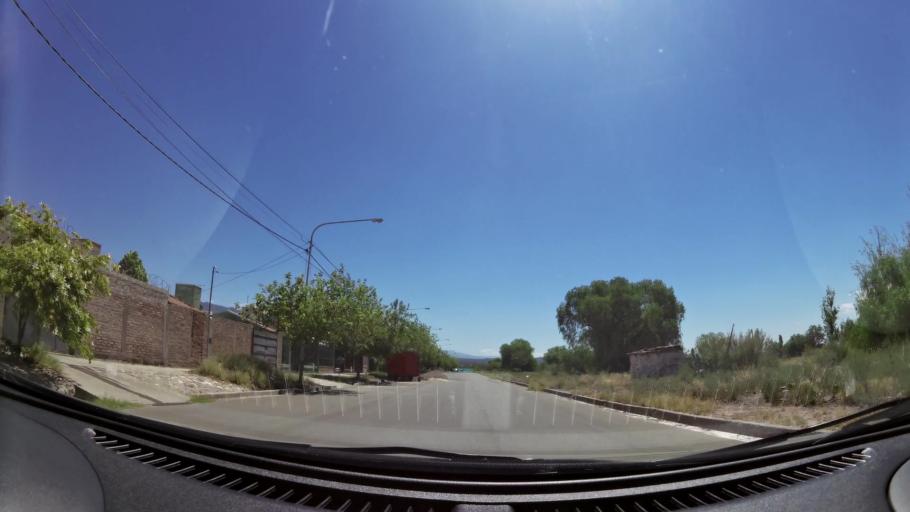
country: AR
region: Mendoza
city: Las Heras
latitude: -32.8405
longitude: -68.8620
